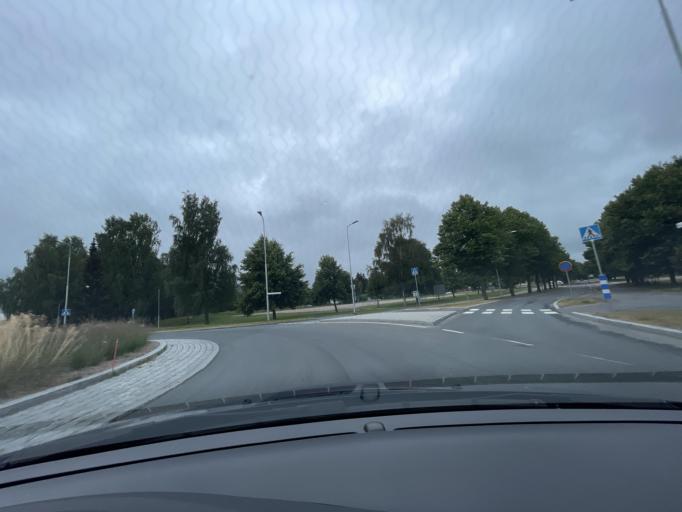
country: FI
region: Haeme
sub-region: Riihimaeki
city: Riihimaeki
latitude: 60.7312
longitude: 24.7680
